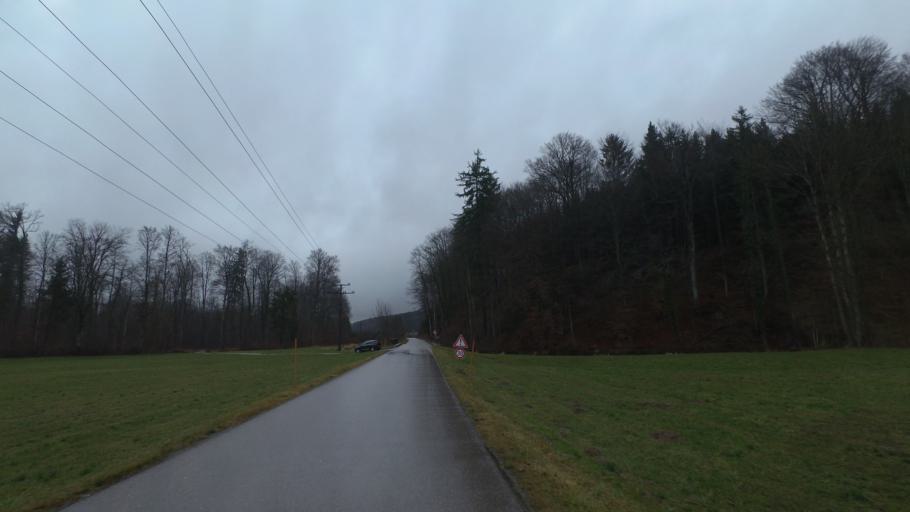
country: DE
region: Bavaria
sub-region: Upper Bavaria
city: Nussdorf
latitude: 47.9109
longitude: 12.6240
